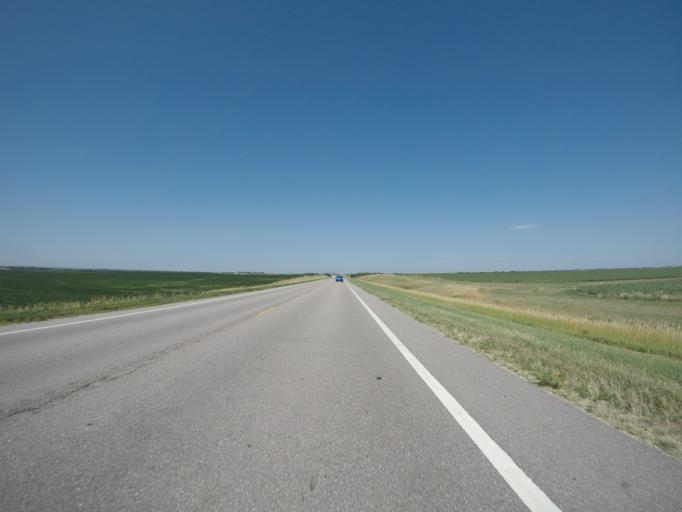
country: US
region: Kansas
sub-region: Cloud County
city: Concordia
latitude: 39.3646
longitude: -97.7506
